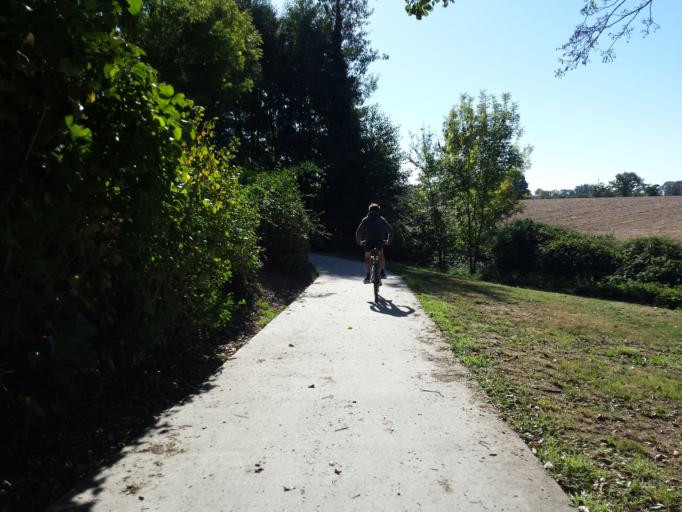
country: FR
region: Pays de la Loire
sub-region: Departement de la Vendee
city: La Ferriere
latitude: 46.7099
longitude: -1.3156
